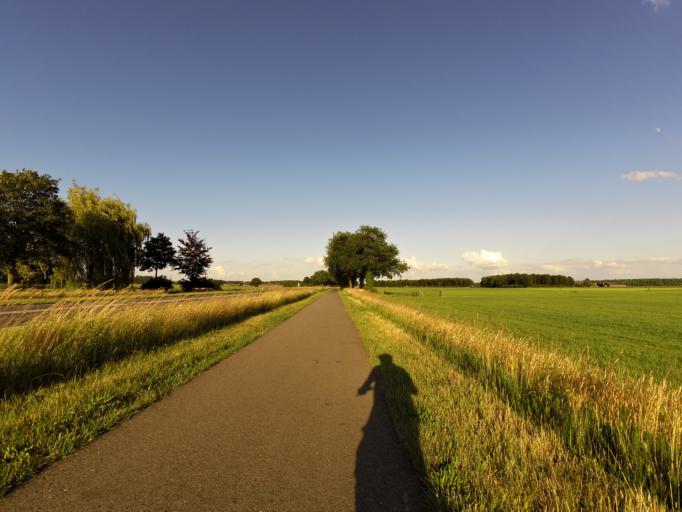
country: NL
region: Gelderland
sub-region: Oude IJsselstreek
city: Wisch
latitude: 51.8881
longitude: 6.4257
